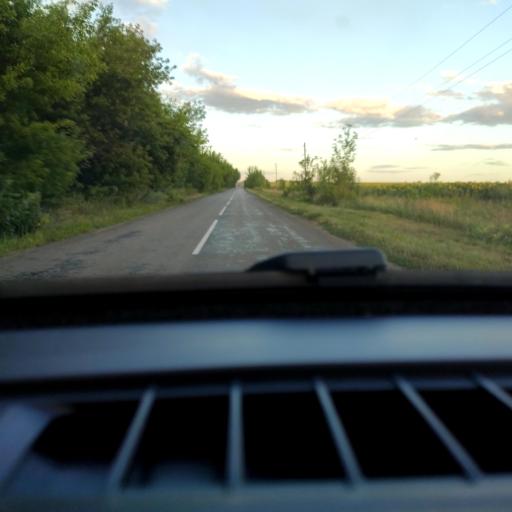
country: RU
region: Voronezj
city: Orlovo
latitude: 51.6434
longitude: 39.7393
